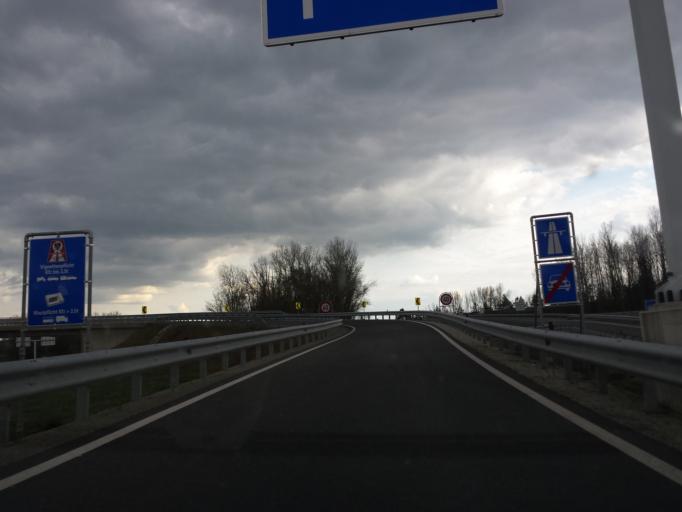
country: AT
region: Lower Austria
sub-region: Politischer Bezirk Sankt Polten
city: Traismauer
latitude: 48.3729
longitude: 15.7142
